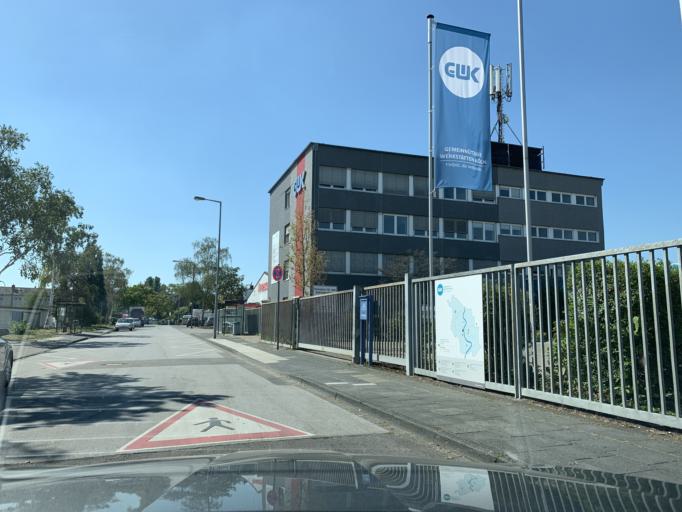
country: DE
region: North Rhine-Westphalia
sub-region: Regierungsbezirk Koln
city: Mengenich
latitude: 51.0069
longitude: 6.8722
